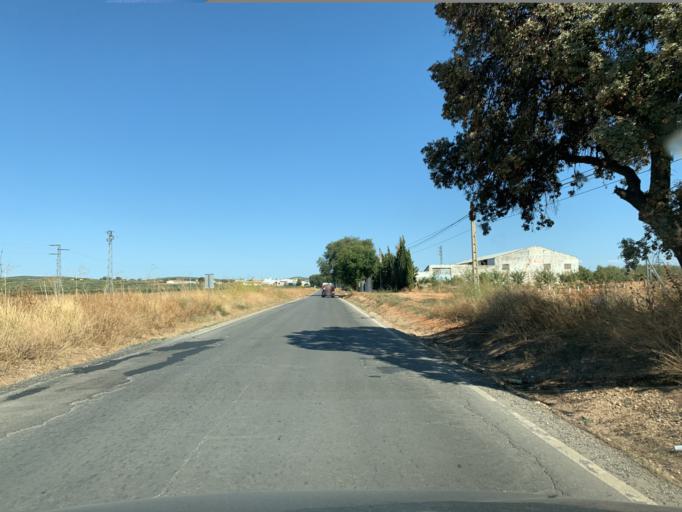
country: ES
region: Andalusia
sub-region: Provincia de Sevilla
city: Marinaleda
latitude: 37.3651
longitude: -4.9715
